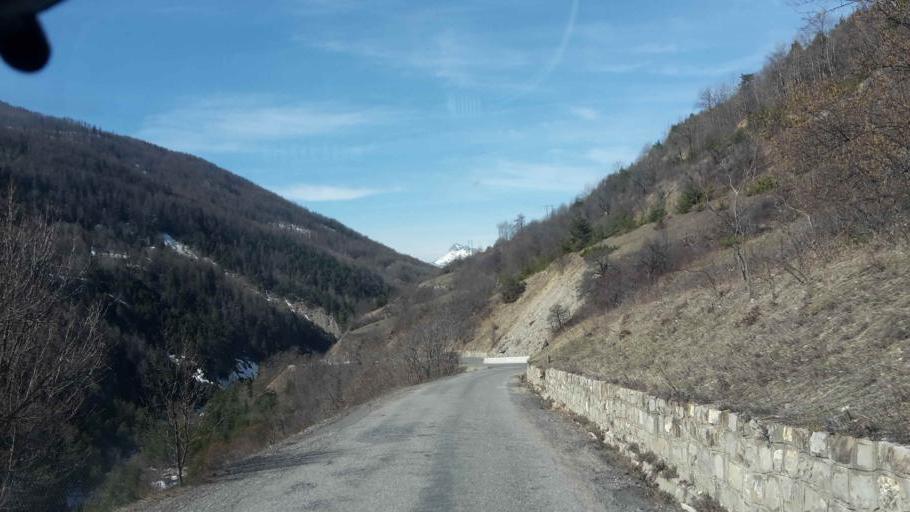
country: FR
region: Provence-Alpes-Cote d'Azur
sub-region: Departement des Hautes-Alpes
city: Embrun
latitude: 44.5500
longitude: 6.5907
